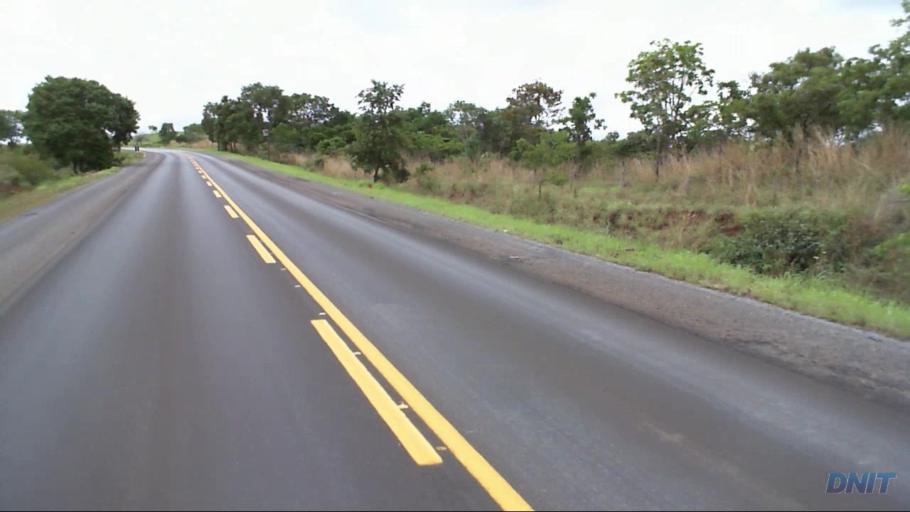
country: BR
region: Goias
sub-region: Padre Bernardo
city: Padre Bernardo
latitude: -15.2161
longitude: -48.5097
